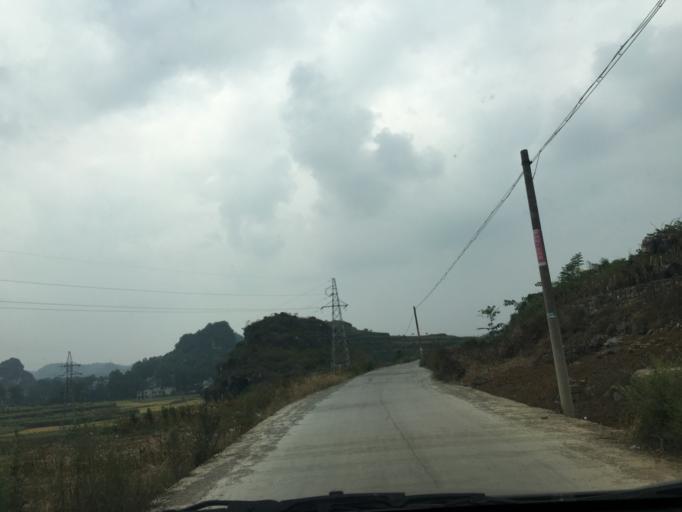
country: CN
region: Guangxi Zhuangzu Zizhiqu
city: Xinzhou
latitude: 25.5303
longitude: 105.6318
